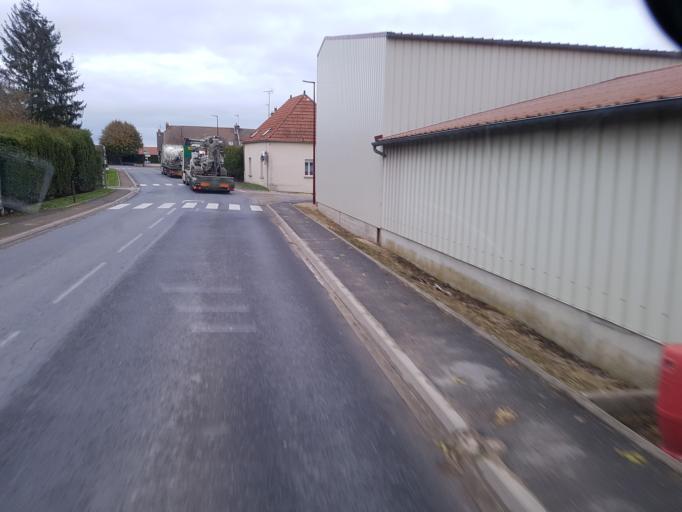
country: FR
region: Champagne-Ardenne
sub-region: Departement de la Marne
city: Sezanne
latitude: 48.6886
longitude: 3.7551
